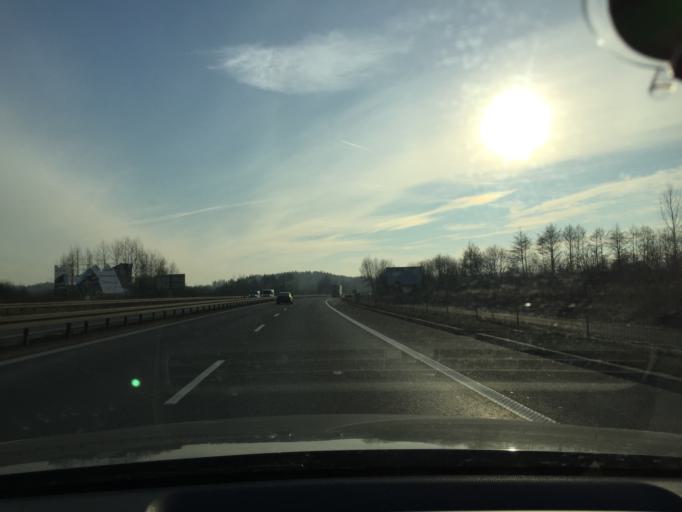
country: PL
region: Lesser Poland Voivodeship
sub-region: Powiat krakowski
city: Kryspinow
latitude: 50.0564
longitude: 19.8097
